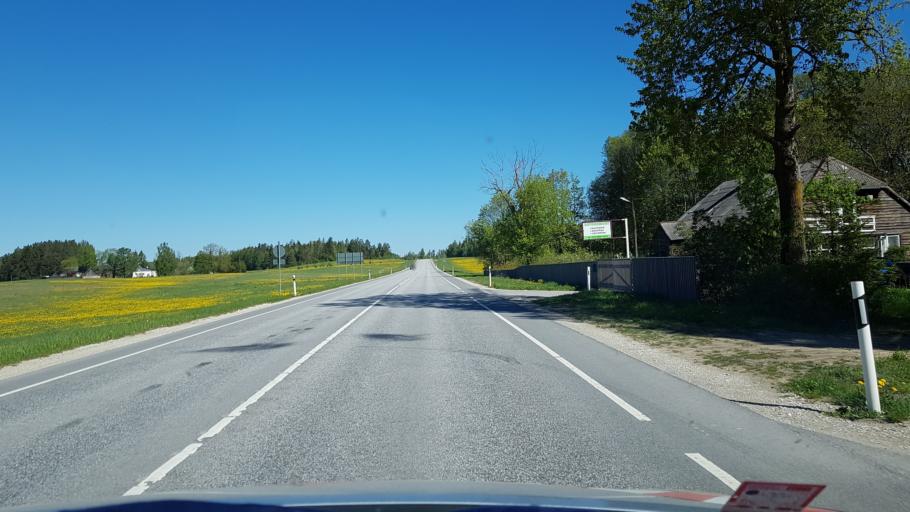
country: EE
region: Tartu
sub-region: Tartu linn
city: Tartu
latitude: 58.5045
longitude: 26.7735
